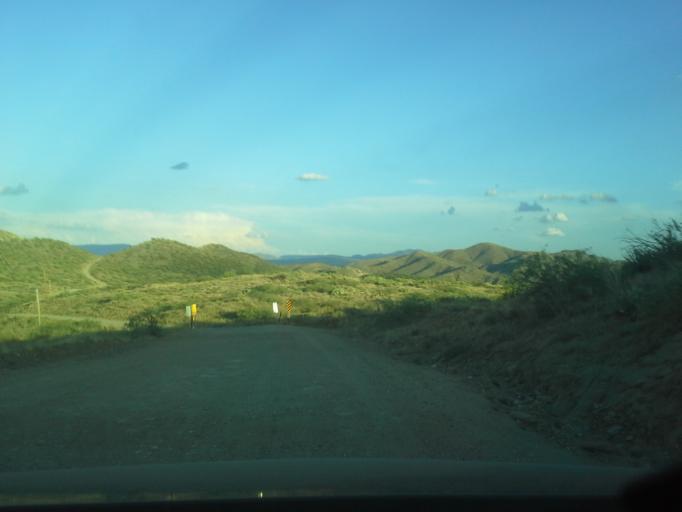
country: US
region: Arizona
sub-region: Yavapai County
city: Spring Valley
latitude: 34.2775
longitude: -112.2287
